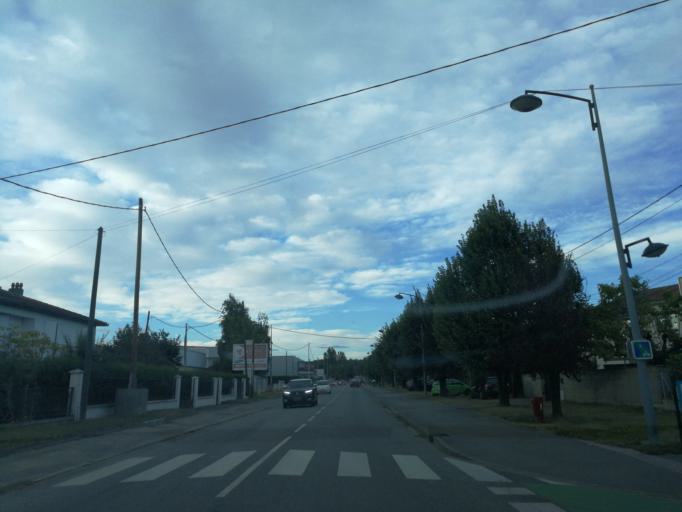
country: FR
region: Midi-Pyrenees
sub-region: Departement de la Haute-Garonne
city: L'Union
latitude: 43.6575
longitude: 1.4706
